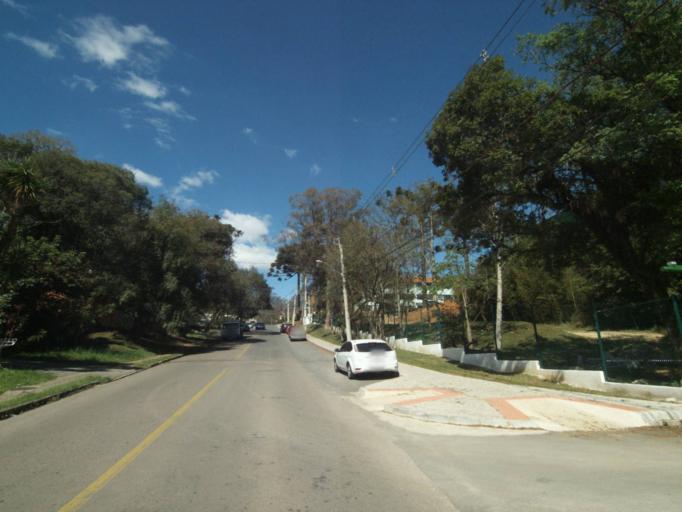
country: BR
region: Parana
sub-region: Curitiba
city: Curitiba
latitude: -25.3914
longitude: -49.2666
